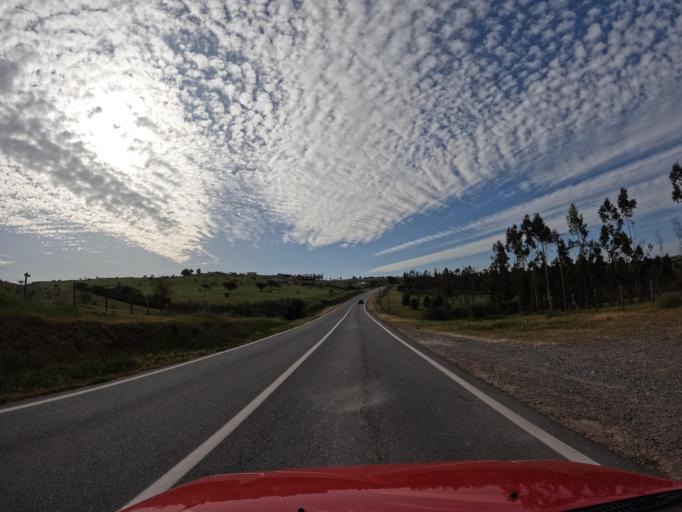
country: CL
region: O'Higgins
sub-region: Provincia de Colchagua
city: Santa Cruz
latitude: -34.2709
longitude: -71.7323
